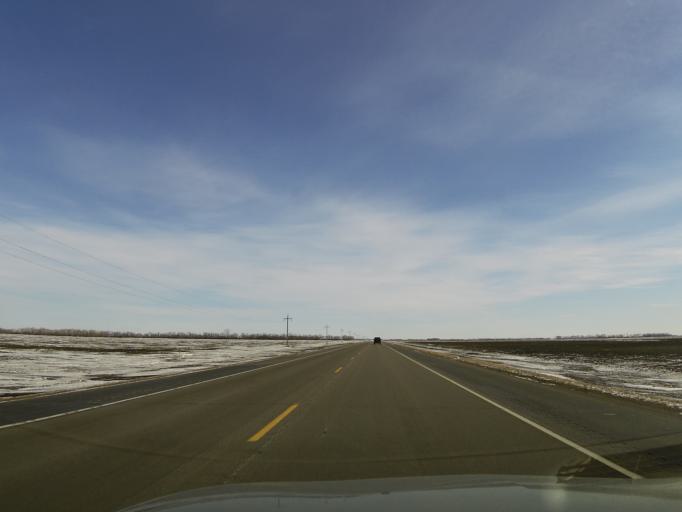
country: US
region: North Dakota
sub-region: Walsh County
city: Grafton
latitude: 48.4123
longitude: -97.3294
